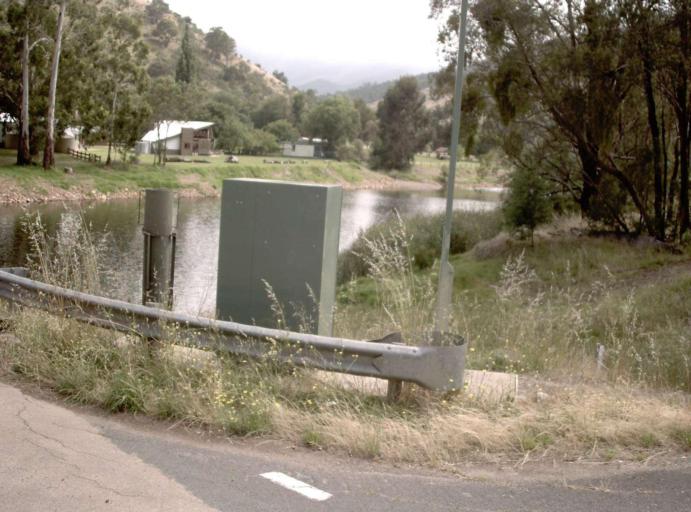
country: AU
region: Victoria
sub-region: Wellington
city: Heyfield
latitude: -37.6296
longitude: 146.6232
